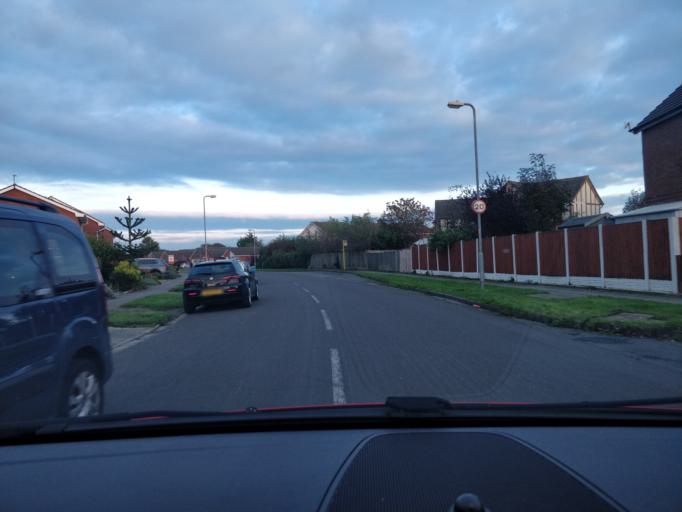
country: GB
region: England
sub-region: Sefton
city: Southport
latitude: 53.6279
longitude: -2.9792
